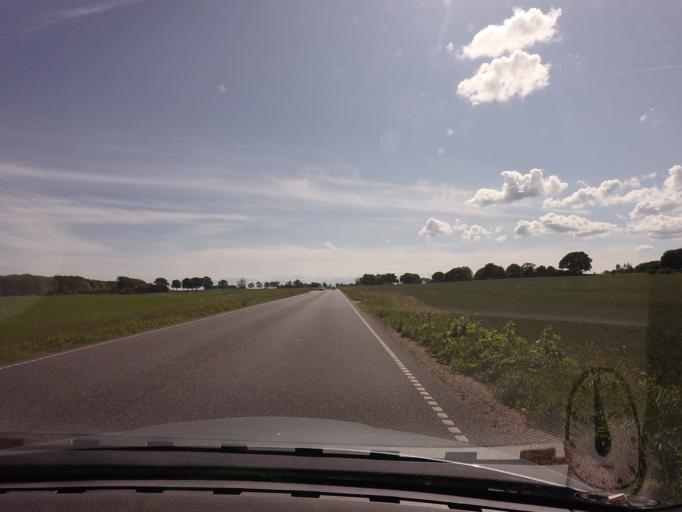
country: DK
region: Central Jutland
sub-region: Syddjurs Kommune
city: Ebeltoft
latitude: 56.3171
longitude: 10.7066
